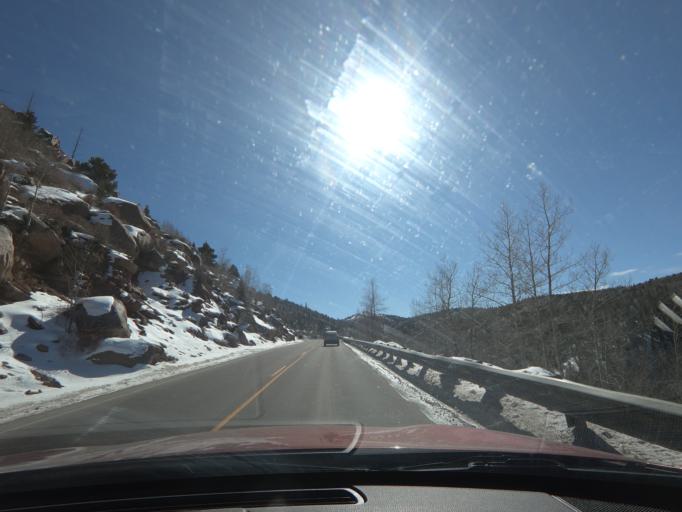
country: US
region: Colorado
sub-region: Teller County
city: Cripple Creek
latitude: 38.8116
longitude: -105.1272
